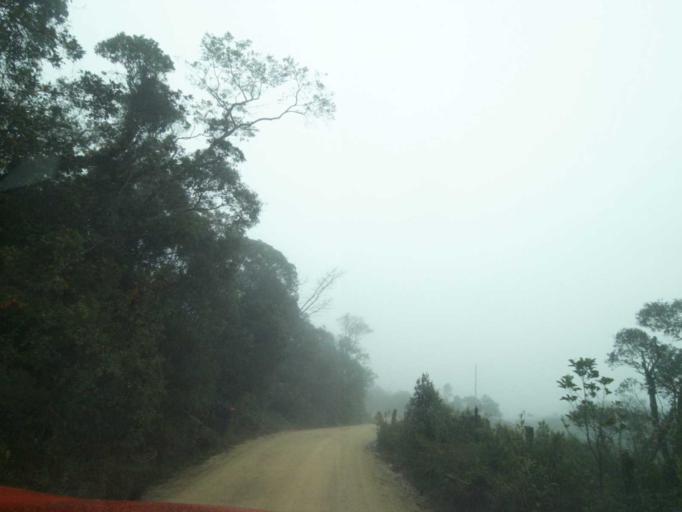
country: BR
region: Santa Catarina
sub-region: Anitapolis
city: Anitapolis
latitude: -27.9117
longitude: -49.1702
